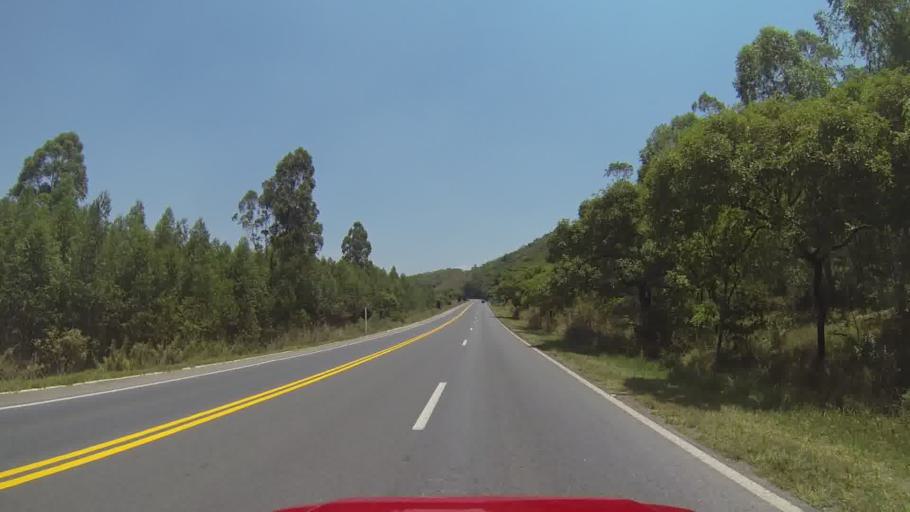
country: BR
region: Minas Gerais
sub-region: Itapecerica
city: Itapecerica
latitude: -20.2969
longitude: -45.1860
